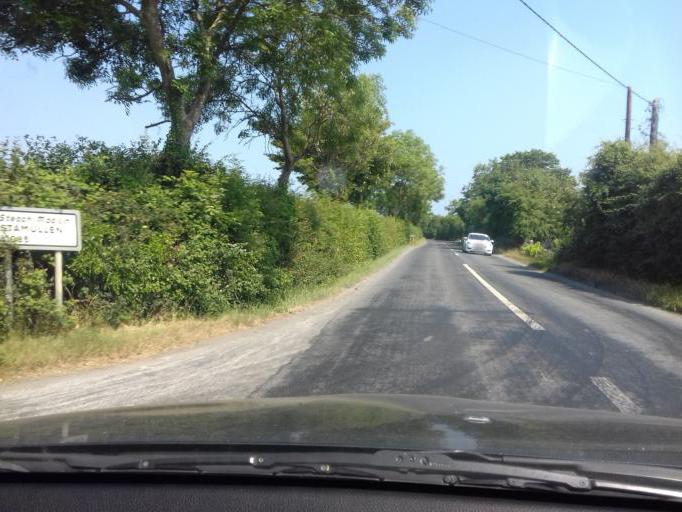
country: IE
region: Leinster
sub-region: An Mhi
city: Stamullin
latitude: 53.5981
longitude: -6.2481
